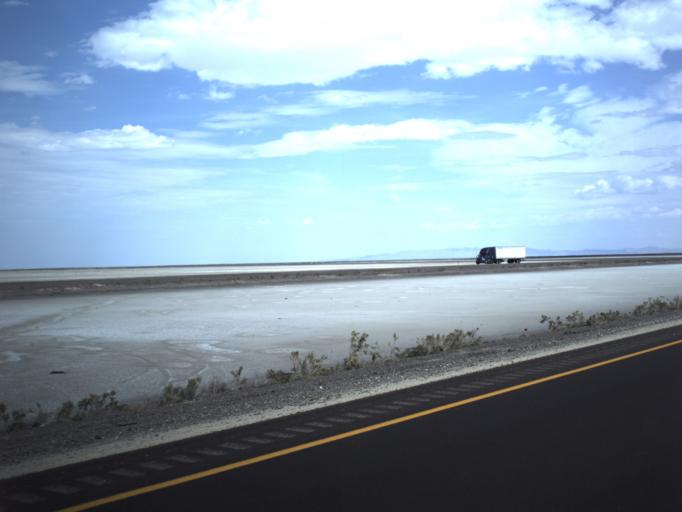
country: US
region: Utah
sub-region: Tooele County
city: Wendover
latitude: 40.7327
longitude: -113.5800
